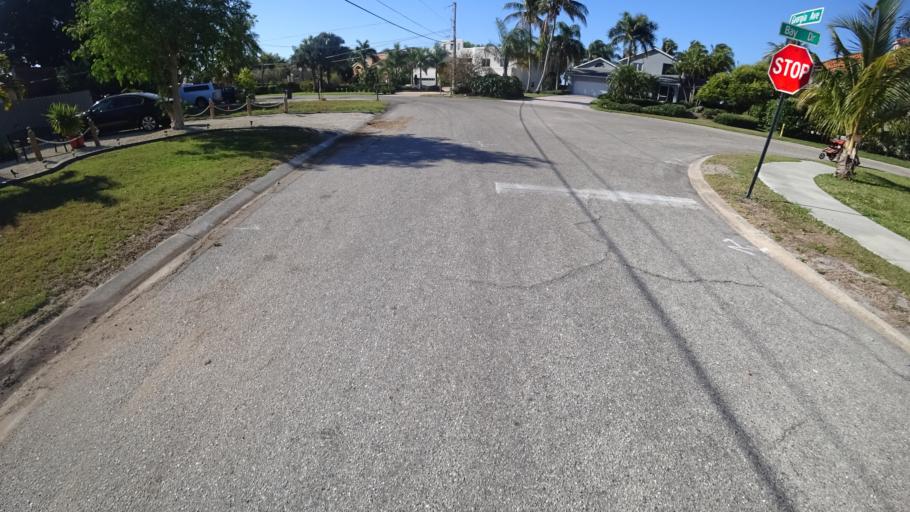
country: US
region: Florida
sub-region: Manatee County
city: Bayshore Gardens
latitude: 27.4196
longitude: -82.5901
